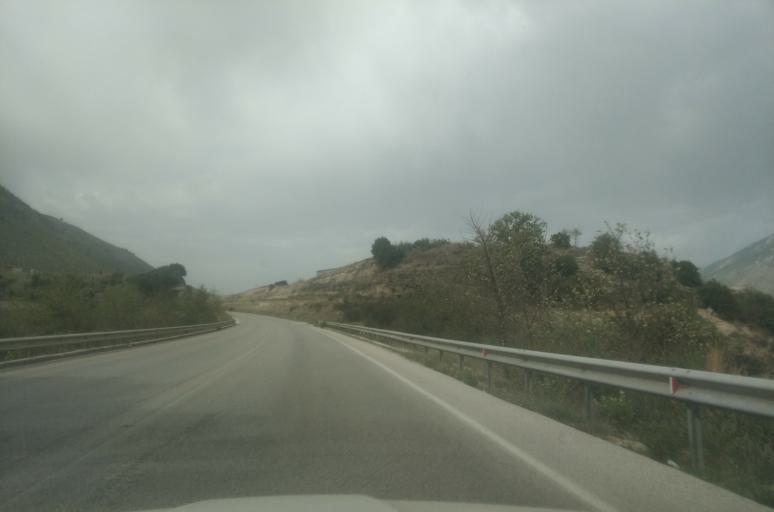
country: AL
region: Gjirokaster
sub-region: Rrethi i Tepelenes
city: Tepelene
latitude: 40.2663
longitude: 20.0500
